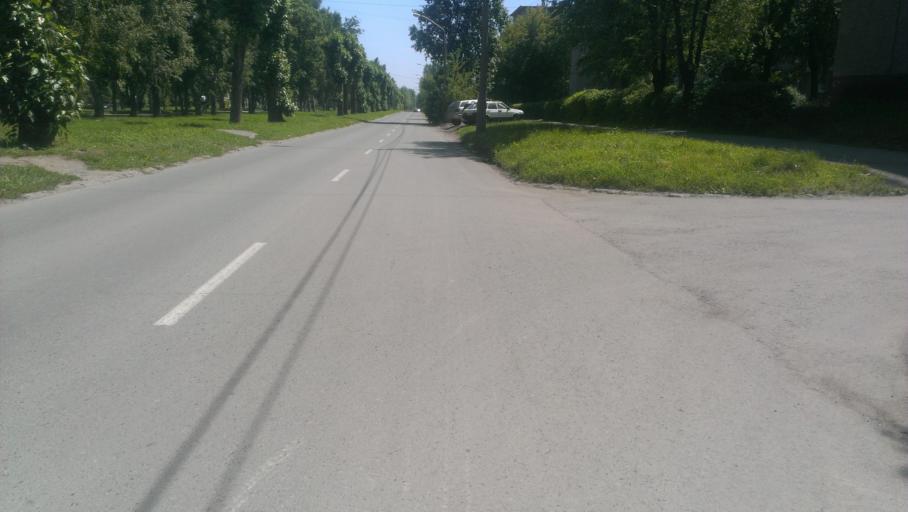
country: RU
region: Altai Krai
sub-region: Gorod Barnaulskiy
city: Barnaul
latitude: 53.3621
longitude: 83.7092
